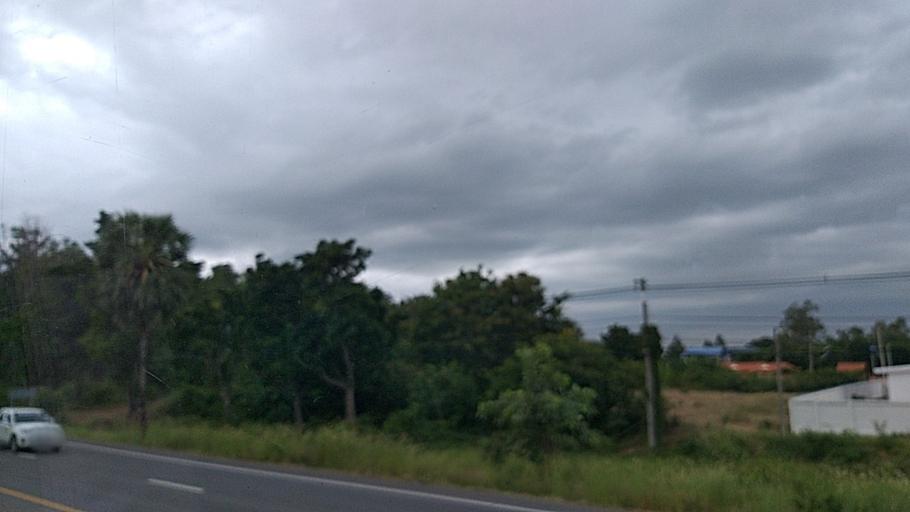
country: TH
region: Khon Kaen
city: Ban Phai
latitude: 16.0335
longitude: 102.7120
